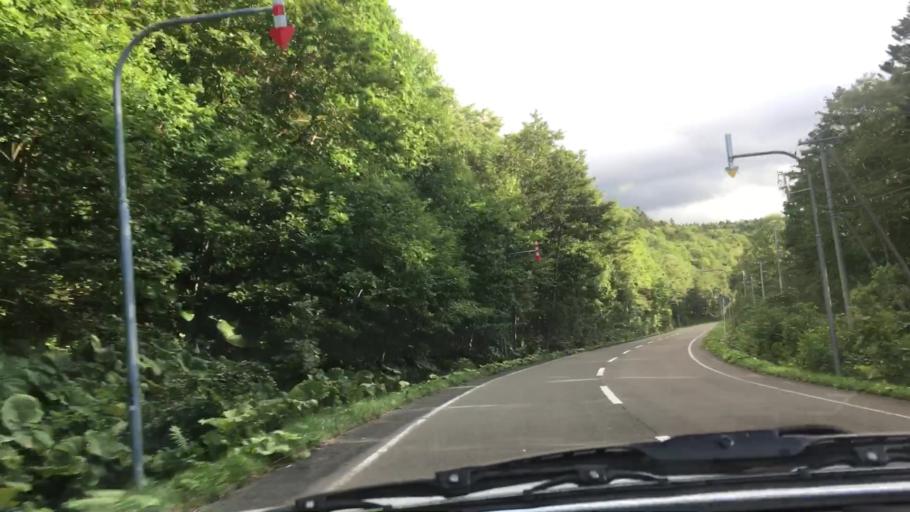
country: JP
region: Hokkaido
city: Shimo-furano
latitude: 43.0970
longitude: 142.6860
